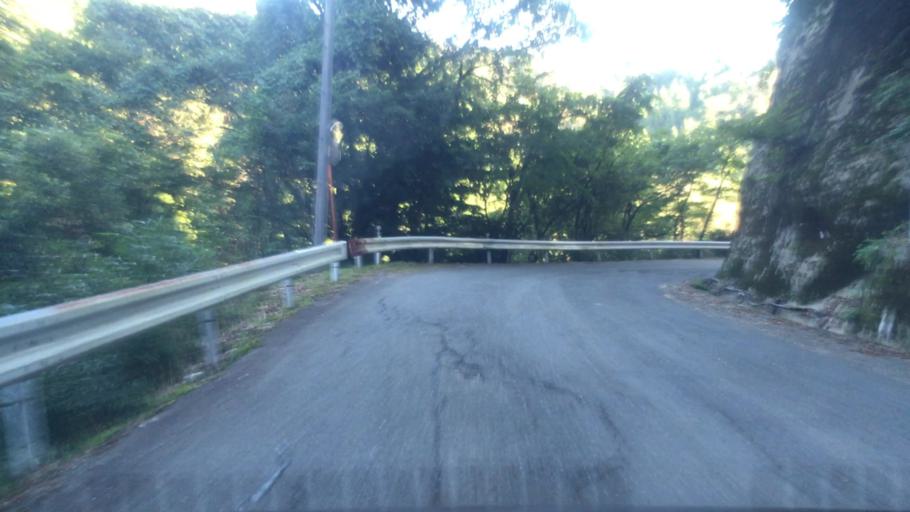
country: JP
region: Hyogo
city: Toyooka
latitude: 35.6113
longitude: 134.8326
